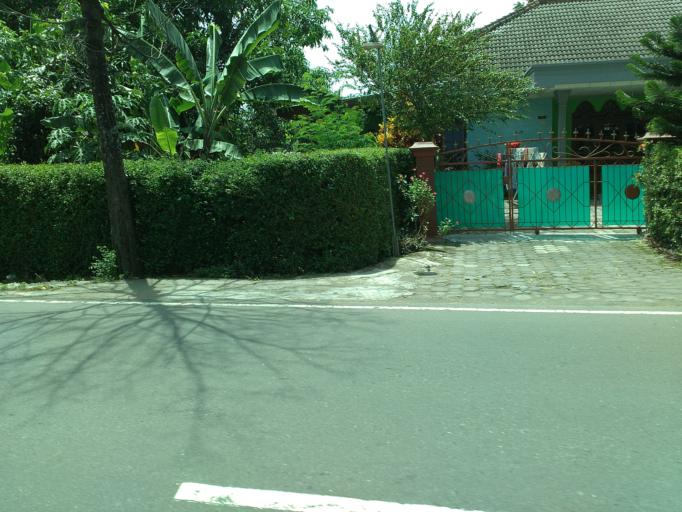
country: ID
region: Central Java
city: Klaten
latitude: -7.6895
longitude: 110.6078
